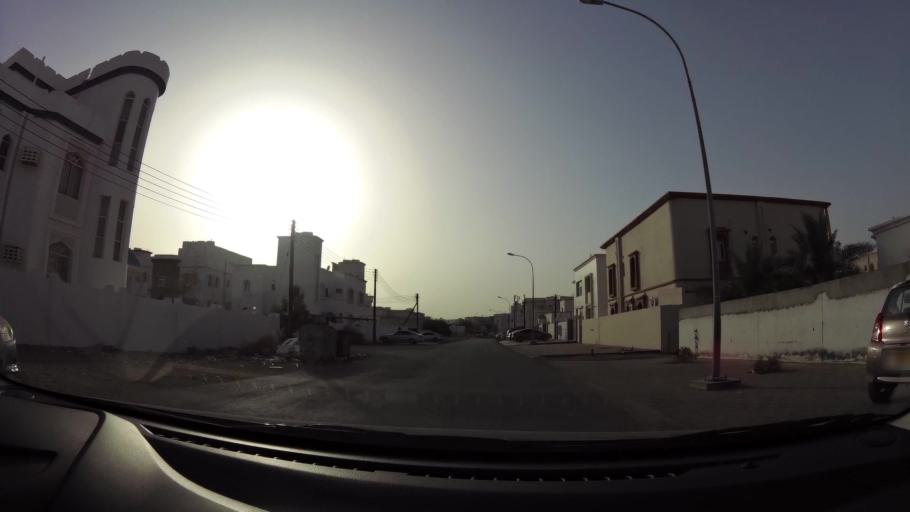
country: OM
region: Muhafazat Masqat
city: Bawshar
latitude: 23.5317
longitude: 58.3485
